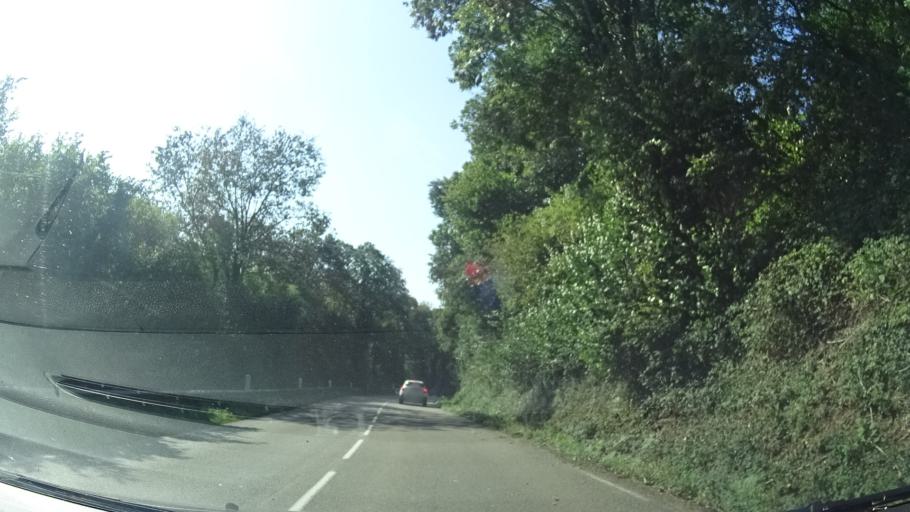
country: FR
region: Brittany
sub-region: Departement du Finistere
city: Douarnenez
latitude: 48.0936
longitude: -4.2883
